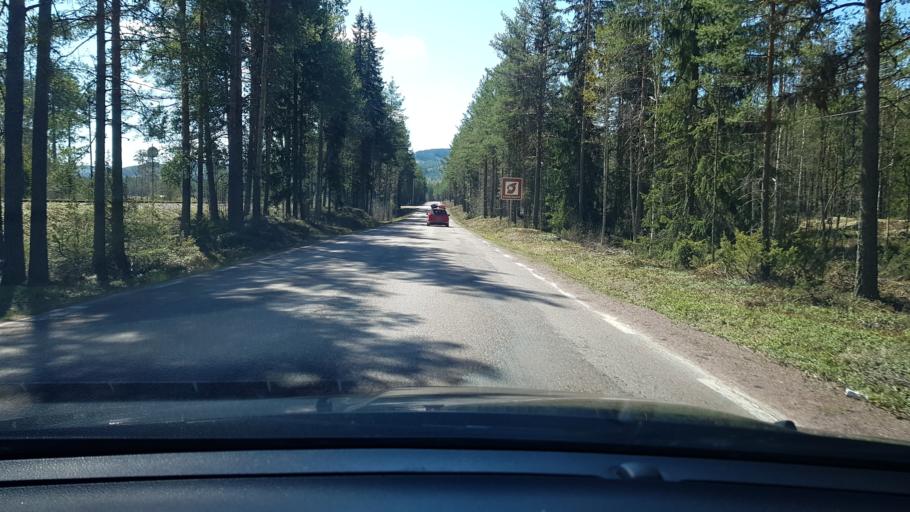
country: SE
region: Dalarna
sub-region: Alvdalens Kommun
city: AElvdalen
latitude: 61.1308
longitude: 14.1720
